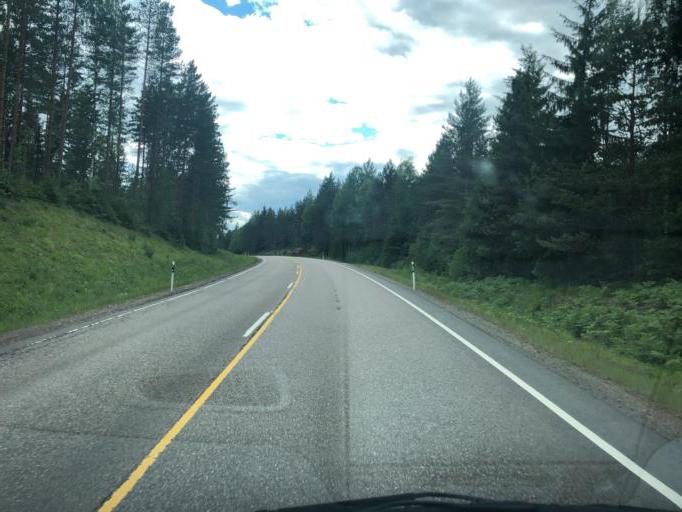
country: FI
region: Southern Savonia
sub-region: Mikkeli
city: Maentyharju
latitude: 61.1484
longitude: 27.1308
